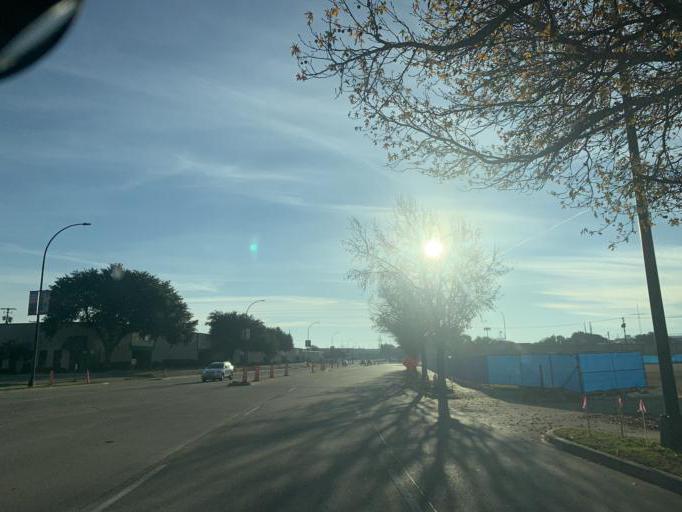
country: US
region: Texas
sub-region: Tarrant County
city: Arlington
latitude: 32.7497
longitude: -97.0799
